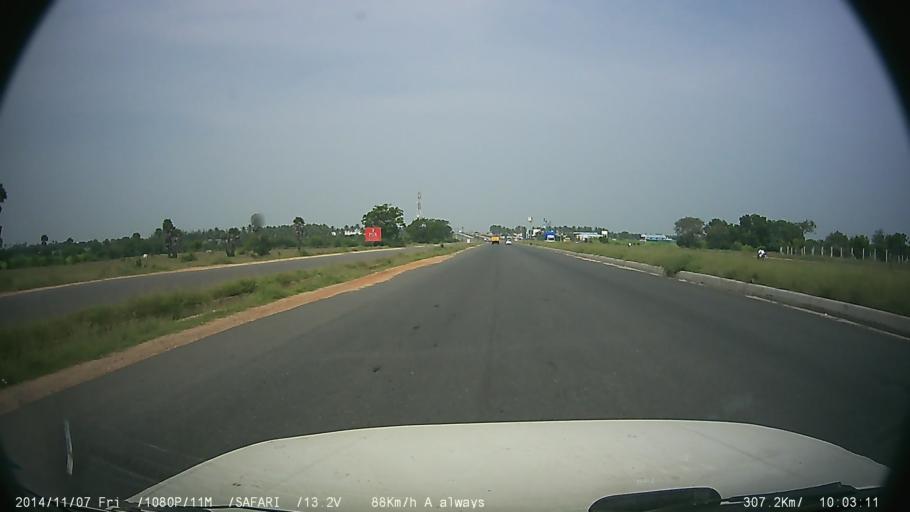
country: IN
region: Tamil Nadu
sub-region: Tiruppur
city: Uttukkuli
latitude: 11.2025
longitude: 77.3972
